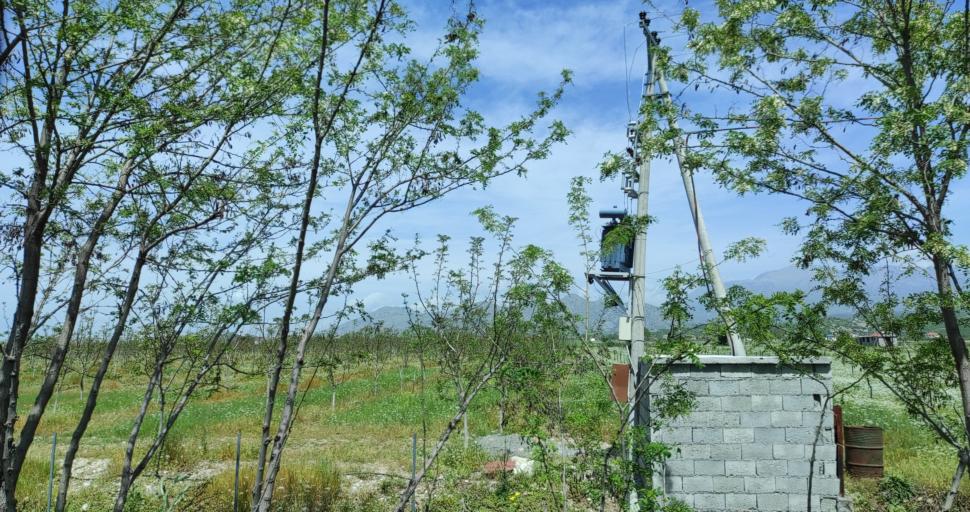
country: AL
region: Shkoder
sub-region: Rrethi i Malesia e Madhe
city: Gruemire
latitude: 42.1424
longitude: 19.5178
